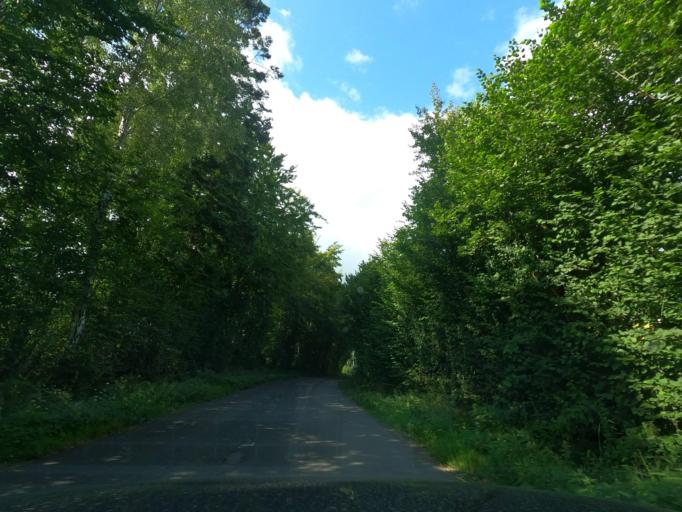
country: FR
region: Lower Normandy
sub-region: Departement de l'Orne
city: Gace
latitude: 48.7835
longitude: 0.2605
